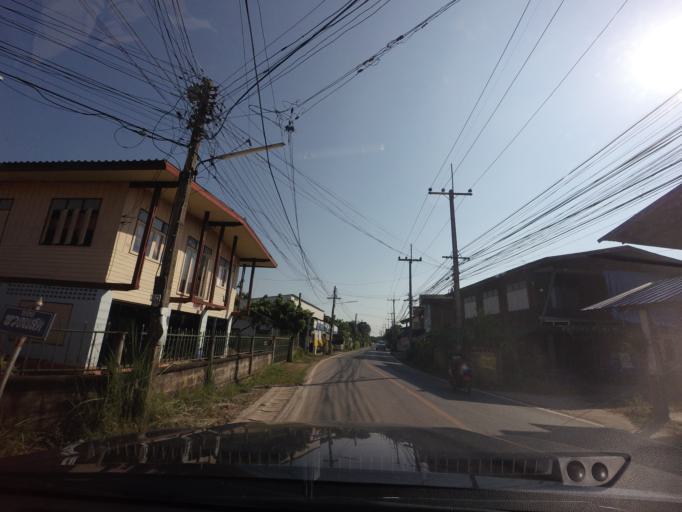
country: TH
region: Nan
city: Nan
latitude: 18.7781
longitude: 100.7850
